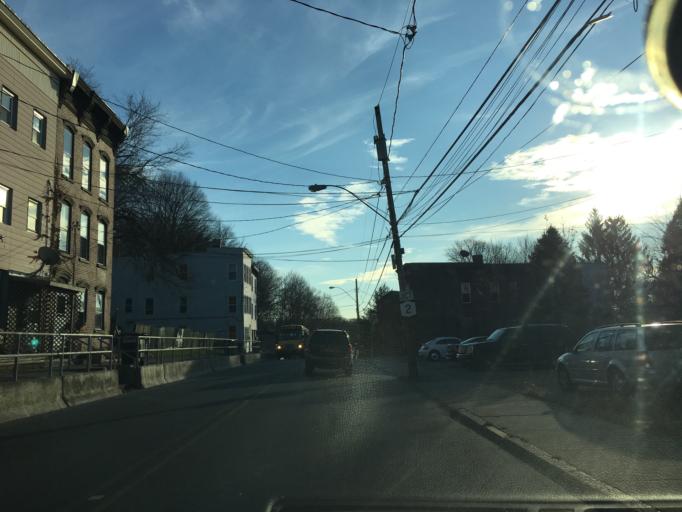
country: US
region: New York
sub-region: Rensselaer County
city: Troy
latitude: 42.7246
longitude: -73.6788
